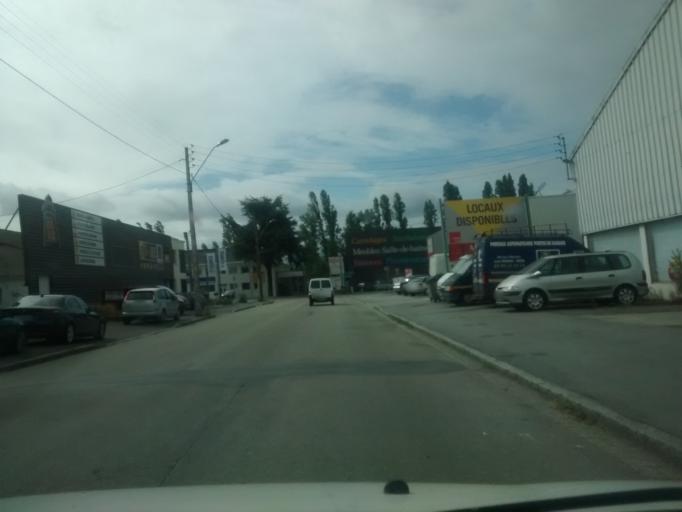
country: FR
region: Brittany
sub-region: Departement d'Ille-et-Vilaine
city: Vezin-le-Coquet
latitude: 48.1027
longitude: -1.7280
